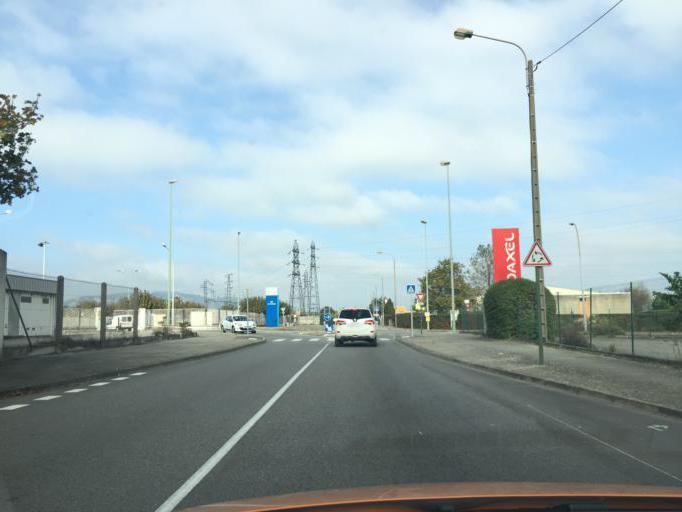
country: FR
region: Rhone-Alpes
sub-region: Departement de la Drome
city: Portes-les-Valence
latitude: 44.8880
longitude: 4.8854
